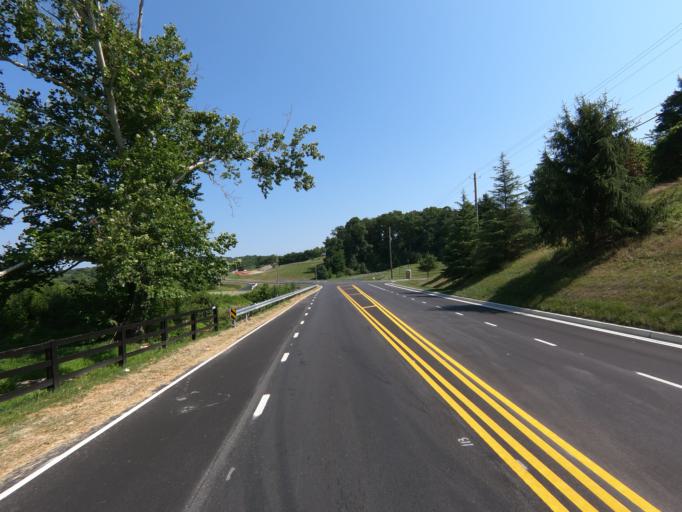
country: US
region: Maryland
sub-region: Frederick County
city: Spring Ridge
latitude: 39.3886
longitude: -77.3252
